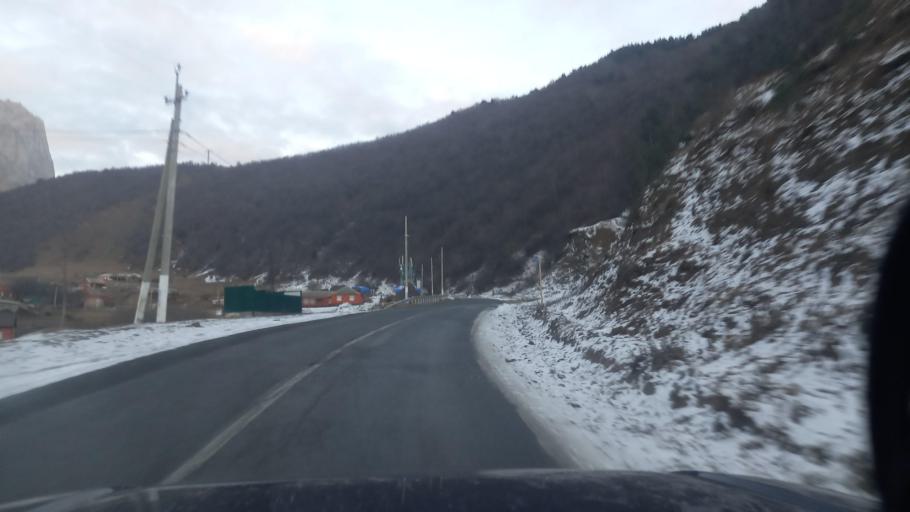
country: RU
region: Ingushetiya
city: Dzhayrakh
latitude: 42.8116
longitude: 44.8073
